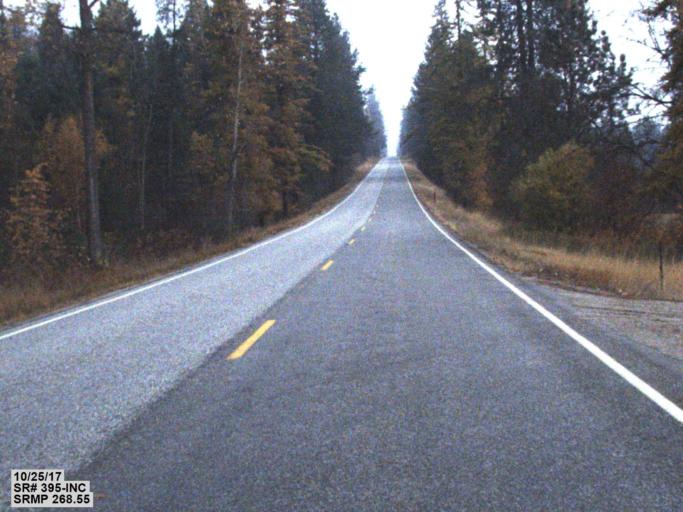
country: CA
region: British Columbia
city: Grand Forks
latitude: 48.9755
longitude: -118.2237
